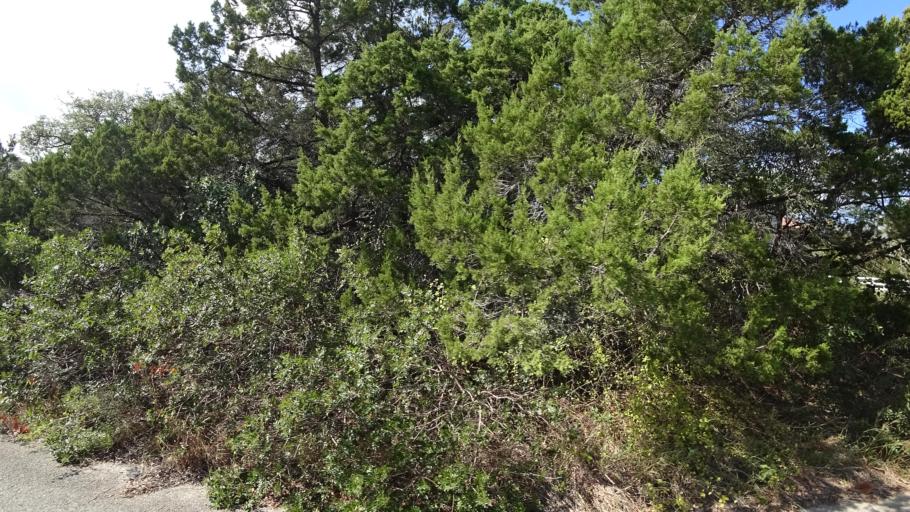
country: US
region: Texas
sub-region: Travis County
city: Lost Creek
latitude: 30.3117
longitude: -97.8581
